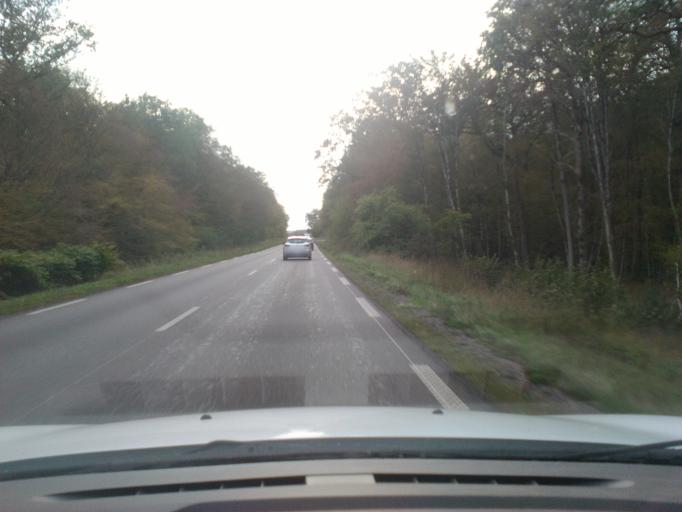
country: FR
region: Lorraine
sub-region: Departement des Vosges
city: Aydoilles
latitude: 48.2654
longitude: 6.5502
